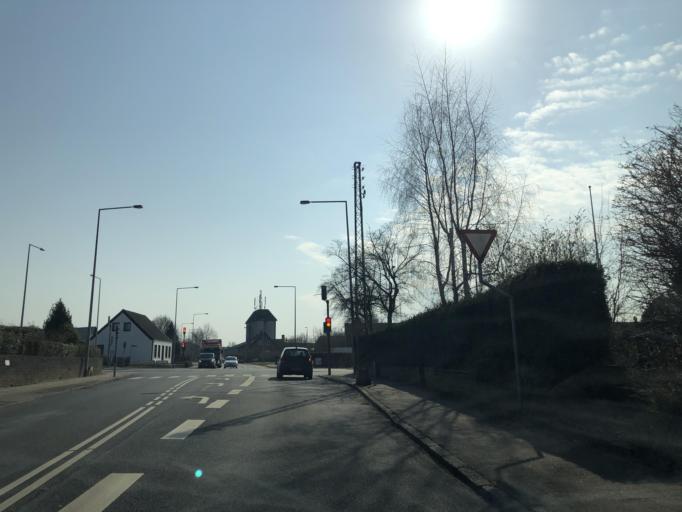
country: DK
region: South Denmark
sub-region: Sonderborg Kommune
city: Nordborg
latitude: 55.0549
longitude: 9.7486
